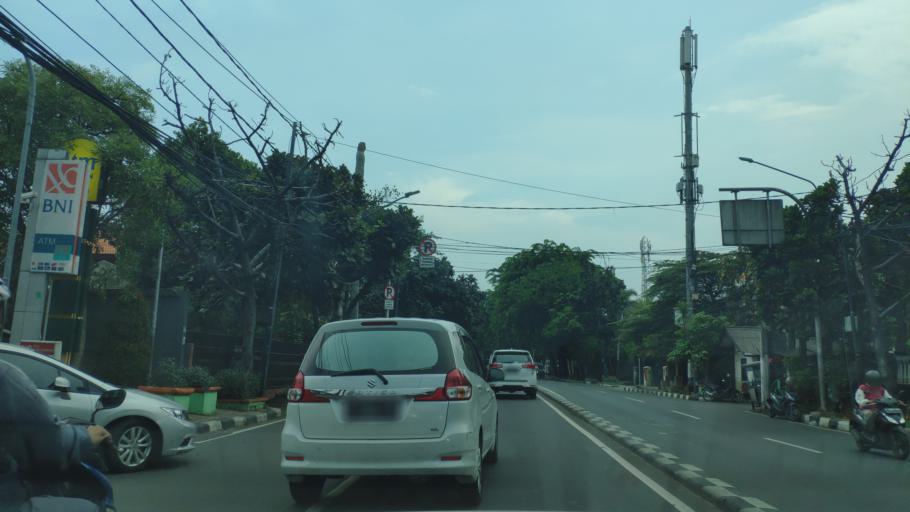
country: ID
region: Jakarta Raya
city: Jakarta
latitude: -6.1893
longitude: 106.7881
